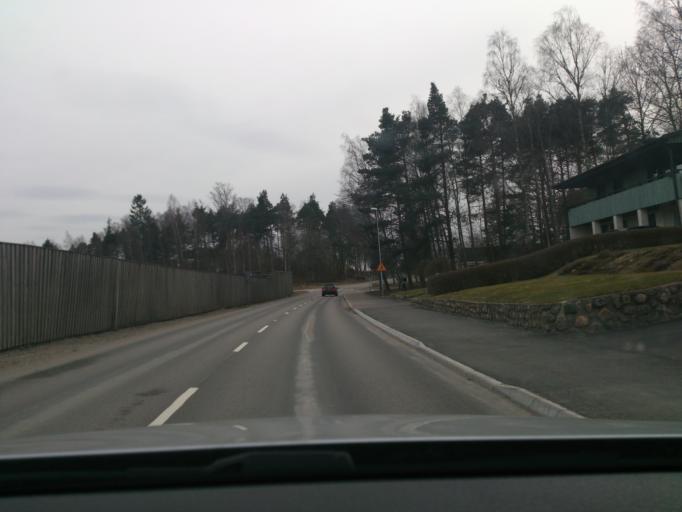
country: SE
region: Kronoberg
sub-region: Alvesta Kommun
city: Moheda
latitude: 57.0087
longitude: 14.5727
